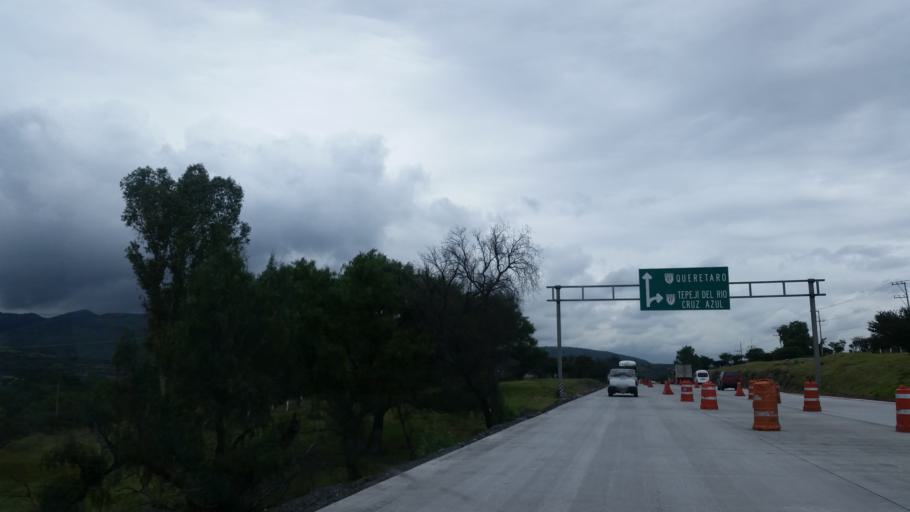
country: MX
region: Hidalgo
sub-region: Tepeji del Rio de Ocampo
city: Santiago Tlapanaloya
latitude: 19.8758
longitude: -99.3375
